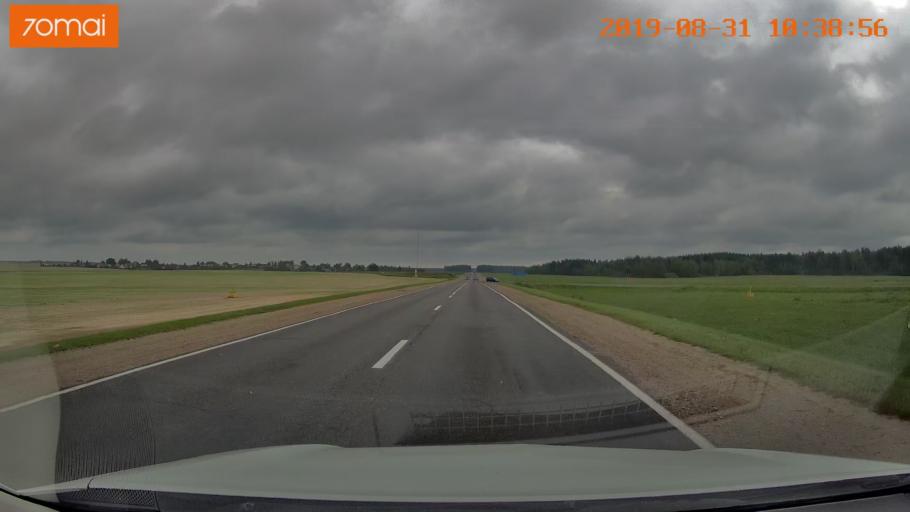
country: BY
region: Mogilev
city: Mahilyow
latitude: 53.9697
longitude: 30.2665
